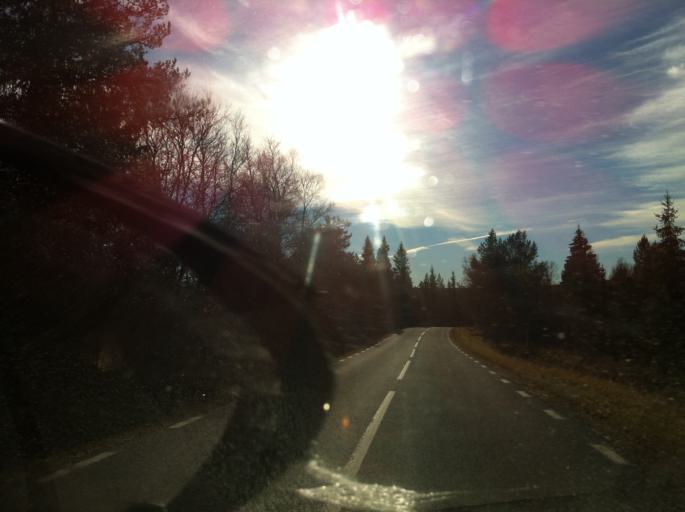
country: NO
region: Hedmark
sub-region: Engerdal
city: Engerdal
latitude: 62.0954
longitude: 12.3122
